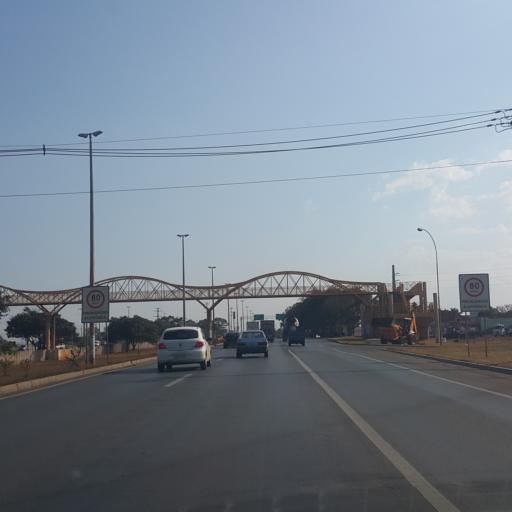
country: BR
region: Federal District
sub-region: Brasilia
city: Brasilia
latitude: -15.8778
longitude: -48.0516
